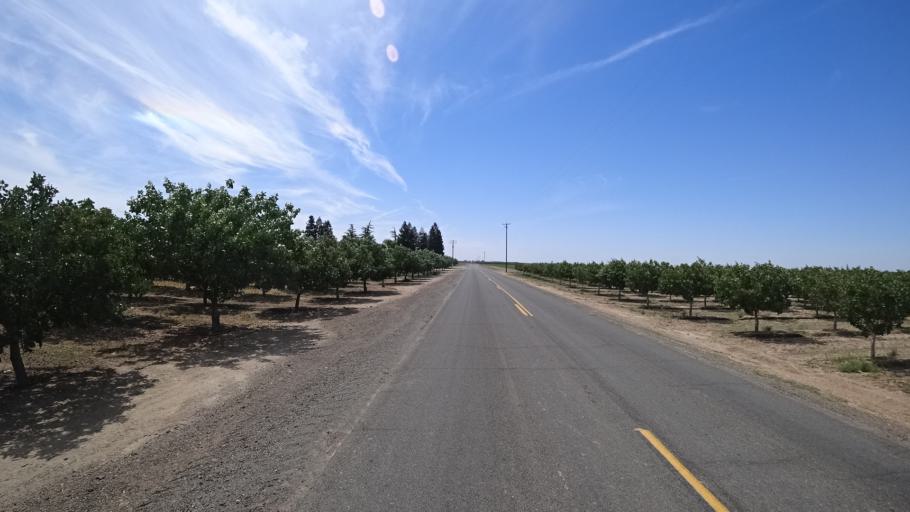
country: US
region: California
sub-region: Kings County
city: Lucerne
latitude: 36.3872
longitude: -119.6910
